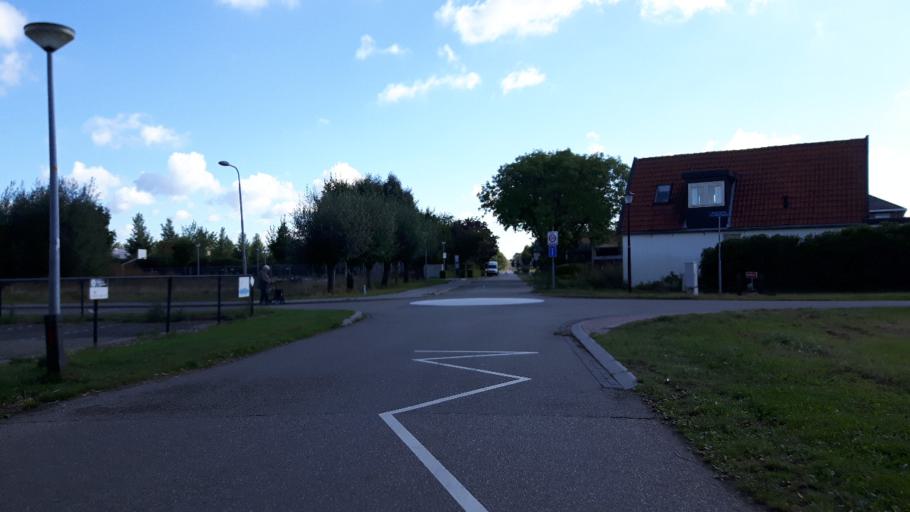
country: NL
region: Gelderland
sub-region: Gemeente Culemborg
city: Culemborg
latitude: 51.9499
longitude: 5.2048
